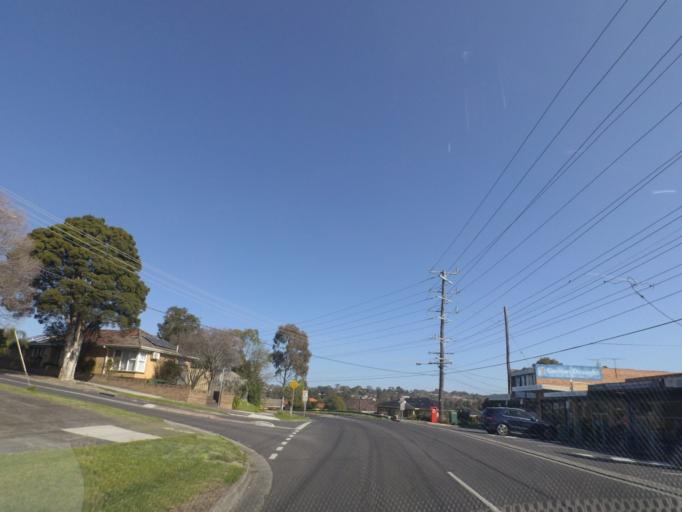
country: AU
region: Victoria
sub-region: Boroondara
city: Balwyn North
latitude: -37.7834
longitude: 145.1031
